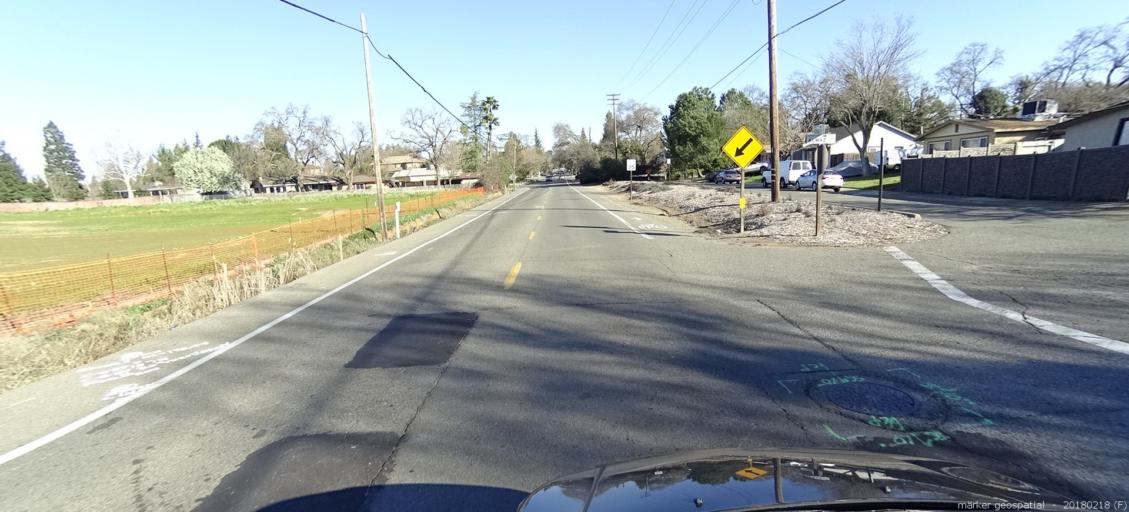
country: US
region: California
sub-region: Sacramento County
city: Orangevale
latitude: 38.6704
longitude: -121.2443
